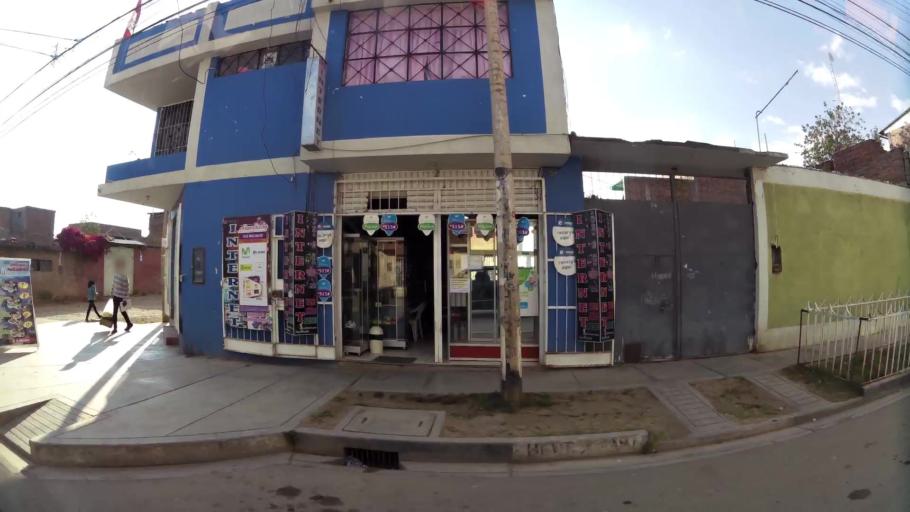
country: PE
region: Junin
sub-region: Provincia de Huancayo
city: El Tambo
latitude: -12.0495
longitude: -75.2183
